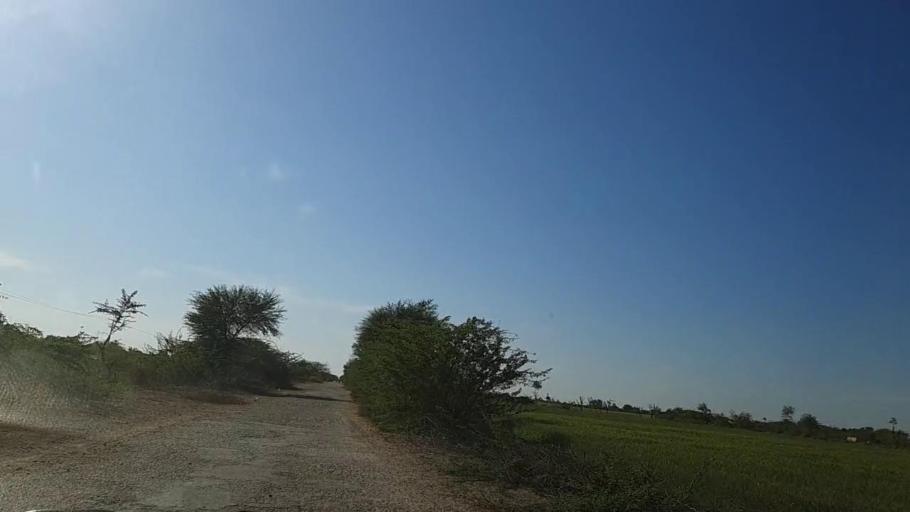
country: PK
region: Sindh
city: Dhoro Naro
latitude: 25.5048
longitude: 69.5277
